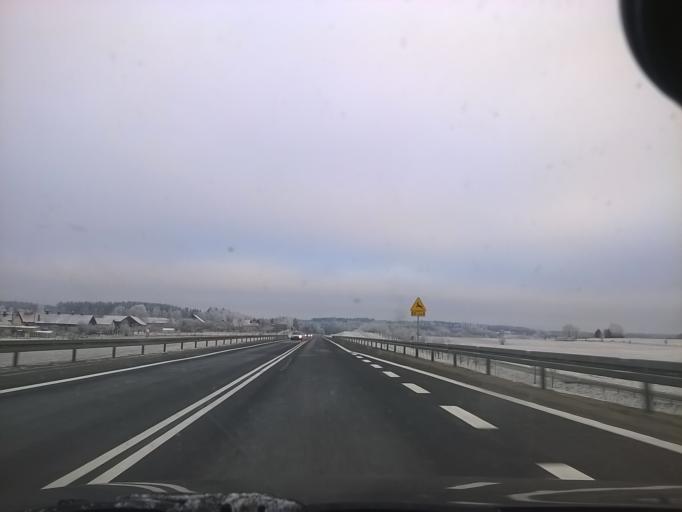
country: PL
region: Warmian-Masurian Voivodeship
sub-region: Powiat olsztynski
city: Barczewo
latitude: 53.8379
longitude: 20.7039
